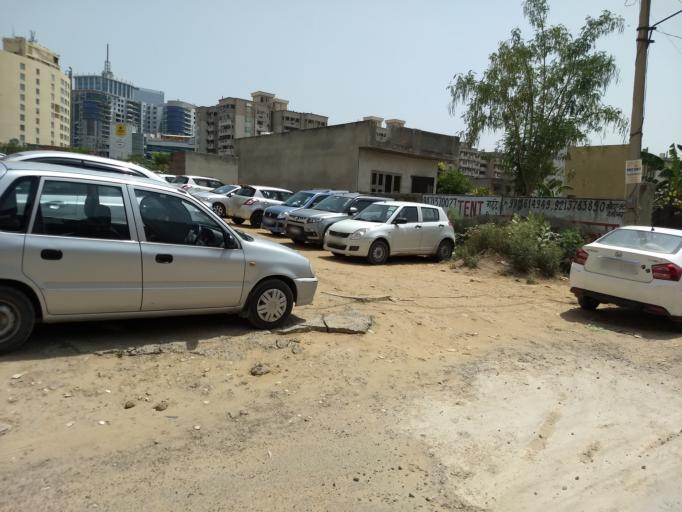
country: IN
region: Haryana
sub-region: Gurgaon
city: Gurgaon
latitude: 28.4570
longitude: 77.0965
